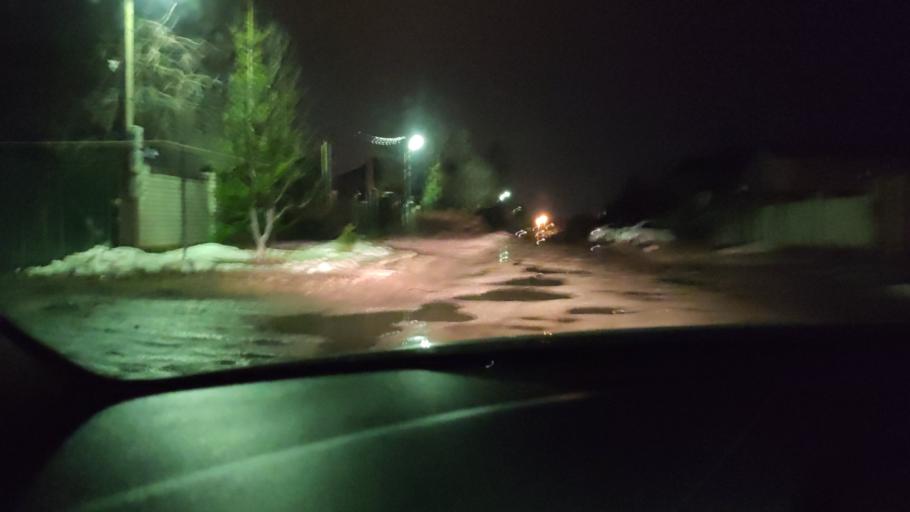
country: RU
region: Tatarstan
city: Vysokaya Gora
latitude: 55.8246
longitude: 49.2313
